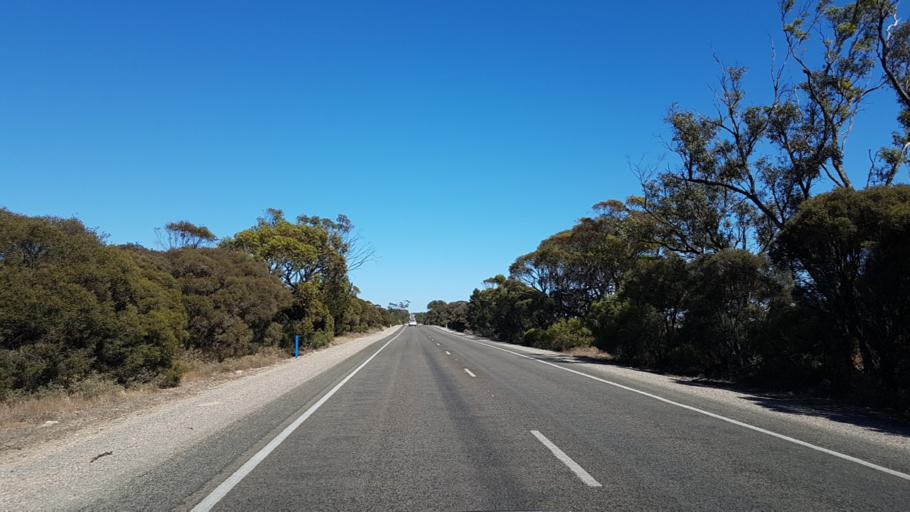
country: AU
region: South Australia
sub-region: Copper Coast
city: Kadina
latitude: -34.0460
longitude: 137.9517
